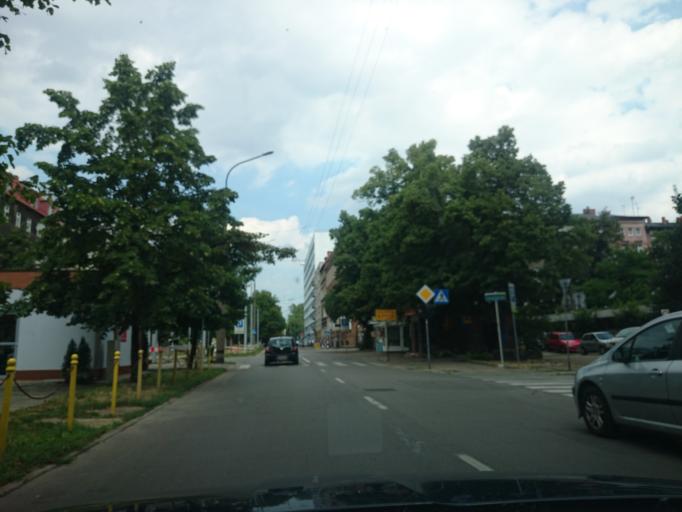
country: PL
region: West Pomeranian Voivodeship
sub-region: Szczecin
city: Szczecin
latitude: 53.4198
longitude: 14.5490
